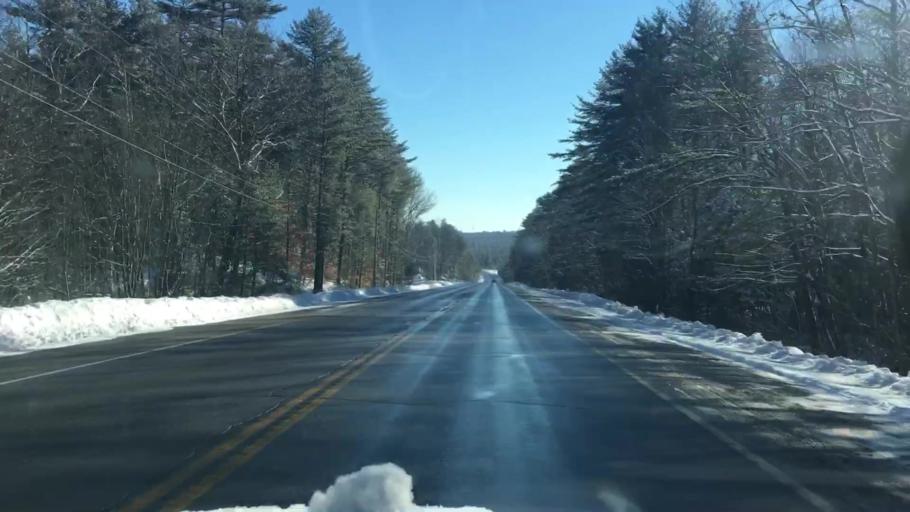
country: US
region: Maine
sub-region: Cumberland County
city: Bridgton
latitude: 44.0168
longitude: -70.6834
